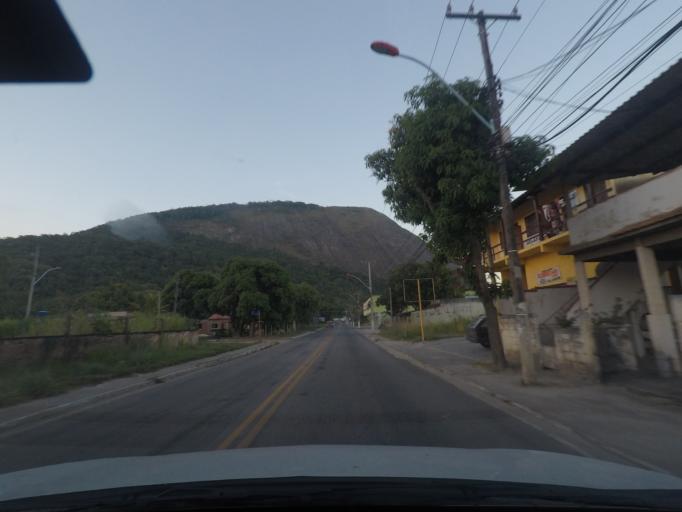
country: BR
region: Rio de Janeiro
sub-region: Marica
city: Marica
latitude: -22.9476
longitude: -42.9623
